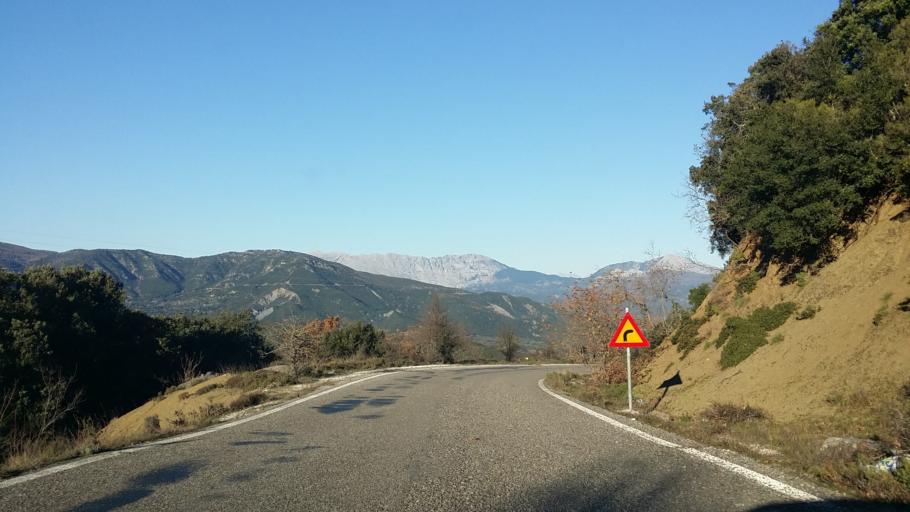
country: GR
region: West Greece
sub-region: Nomos Aitolias kai Akarnanias
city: Sardinia
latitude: 38.8546
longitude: 21.3076
